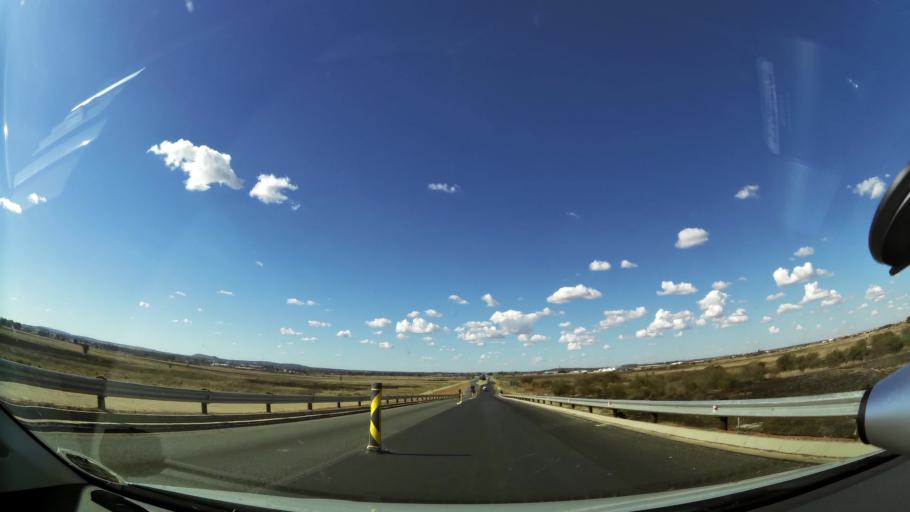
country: ZA
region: North-West
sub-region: Dr Kenneth Kaunda District Municipality
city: Klerksdorp
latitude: -26.8734
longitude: 26.6024
